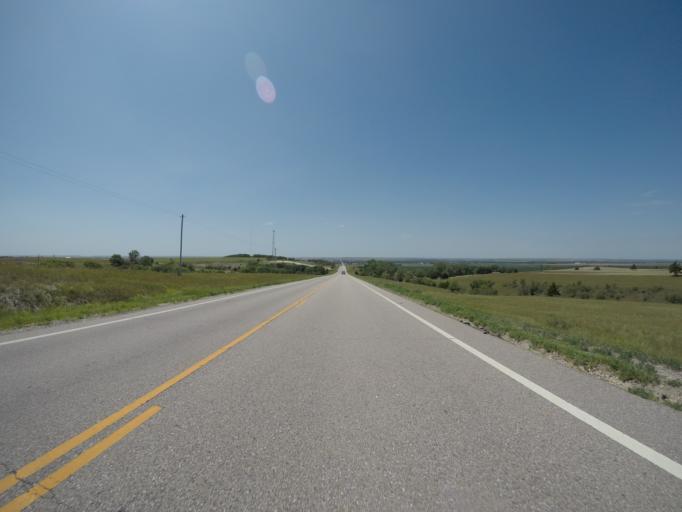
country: US
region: Kansas
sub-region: Osborne County
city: Osborne
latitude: 39.4733
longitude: -98.6943
